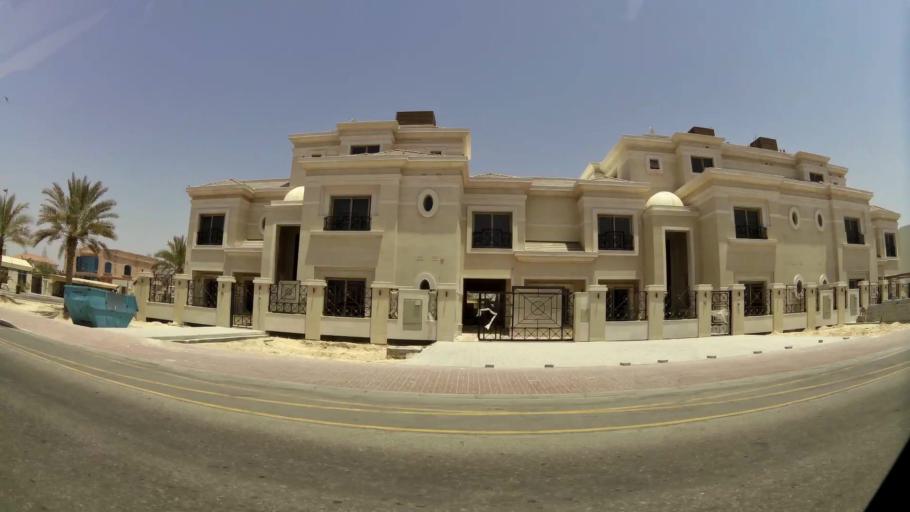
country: AE
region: Dubai
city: Dubai
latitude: 25.2035
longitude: 55.2449
